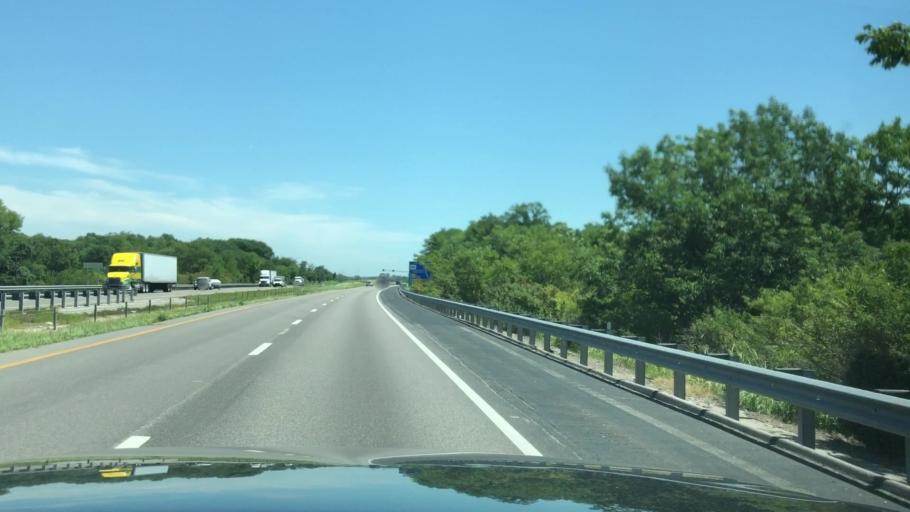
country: US
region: Missouri
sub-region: Saint Louis County
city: Glasgow Village
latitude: 38.7675
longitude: -90.1929
